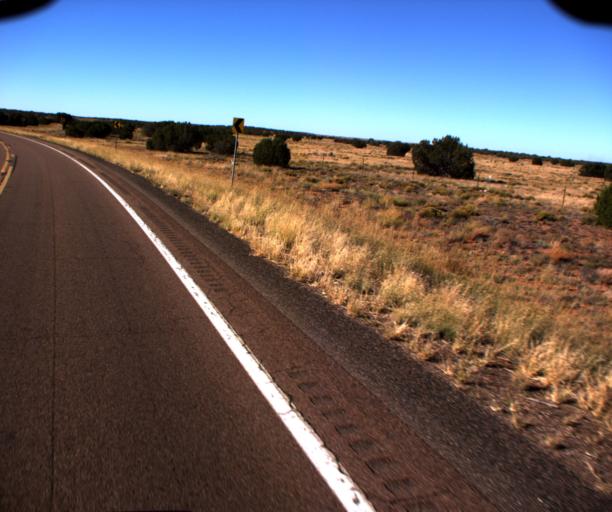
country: US
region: Arizona
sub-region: Navajo County
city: Heber-Overgaard
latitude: 34.5711
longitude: -110.4134
